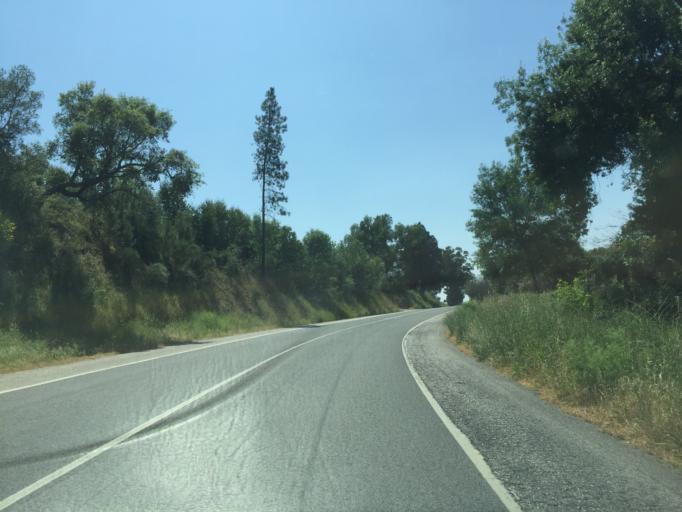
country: PT
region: Santarem
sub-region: Constancia
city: Constancia
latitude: 39.4604
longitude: -8.3461
